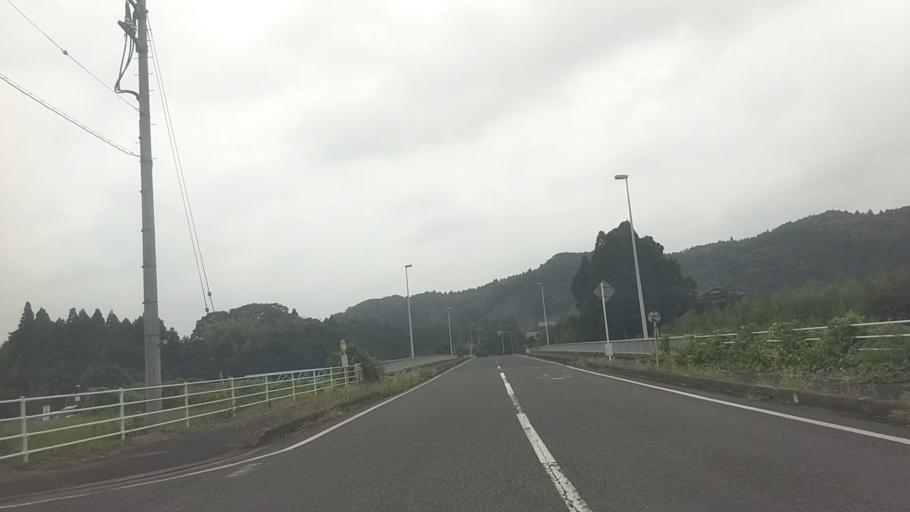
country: JP
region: Chiba
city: Ohara
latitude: 35.2667
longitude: 140.2542
